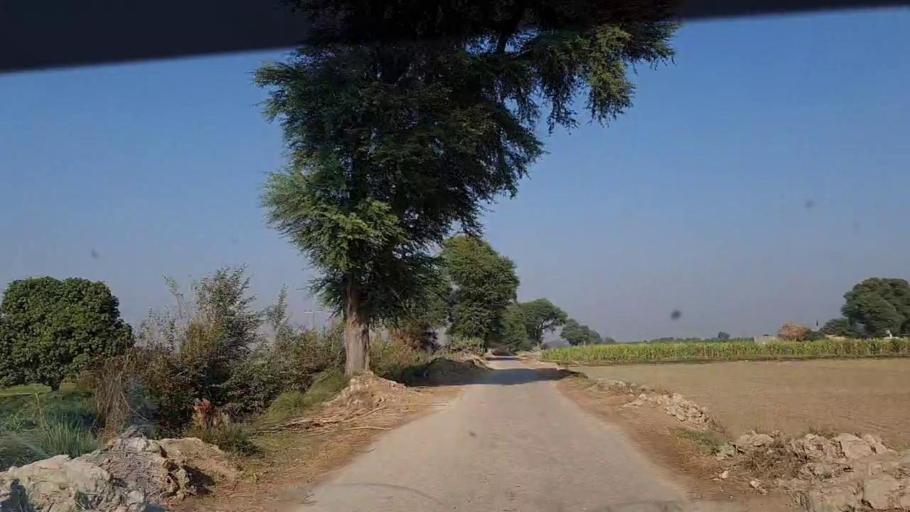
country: PK
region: Sindh
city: Sobhadero
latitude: 27.2421
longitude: 68.3220
